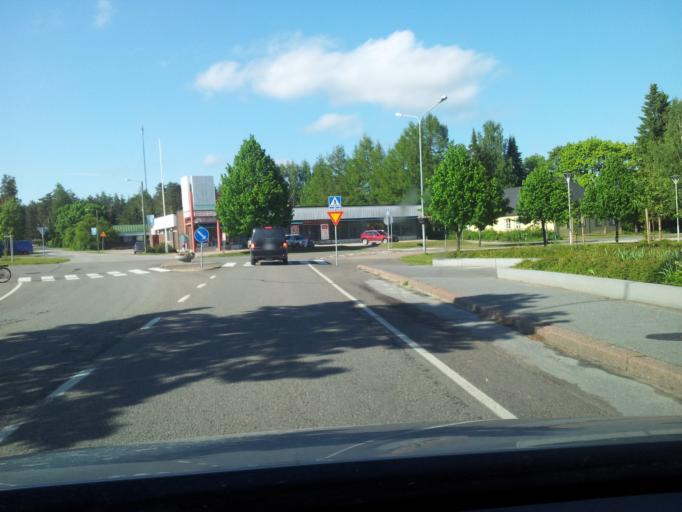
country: FI
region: South Karelia
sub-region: Lappeenranta
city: Taavetti
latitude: 60.9222
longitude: 27.5693
